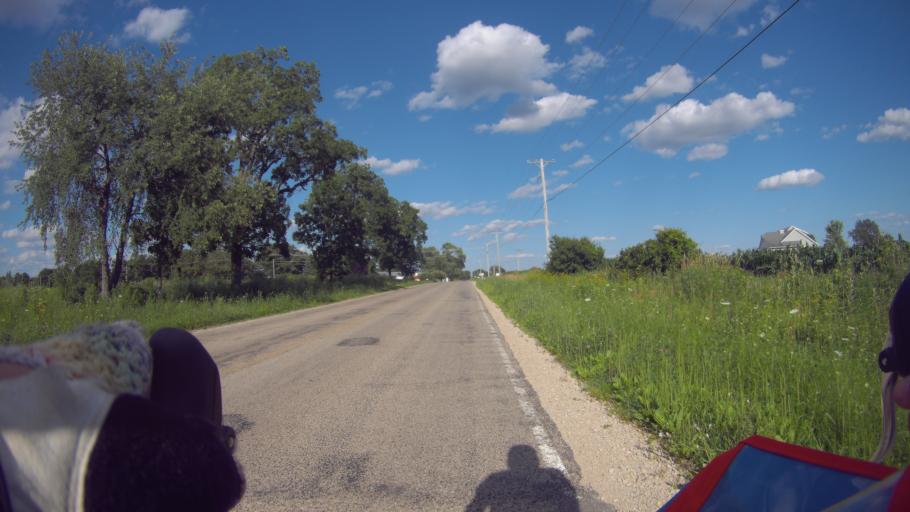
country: US
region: Wisconsin
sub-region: Dane County
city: Oregon
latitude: 42.9351
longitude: -89.3501
